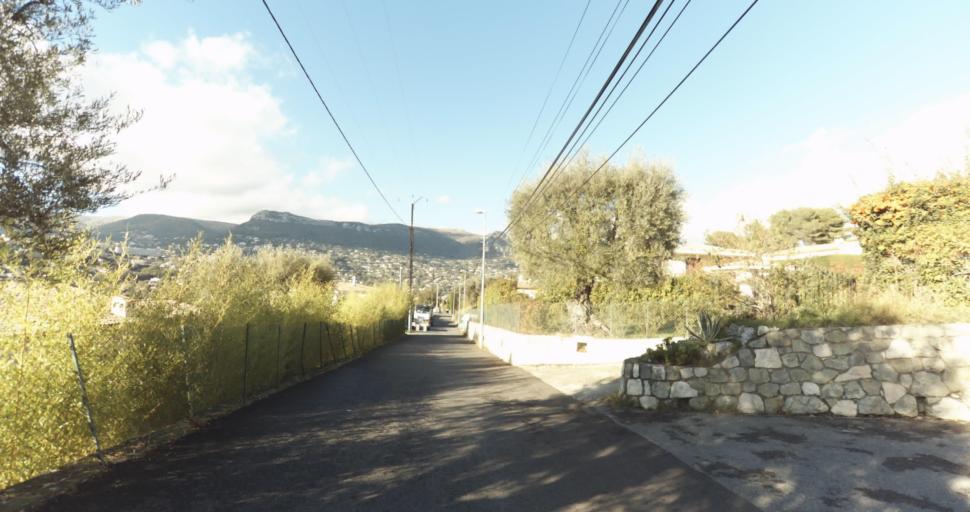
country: FR
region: Provence-Alpes-Cote d'Azur
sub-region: Departement des Alpes-Maritimes
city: La Gaude
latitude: 43.7138
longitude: 7.1340
